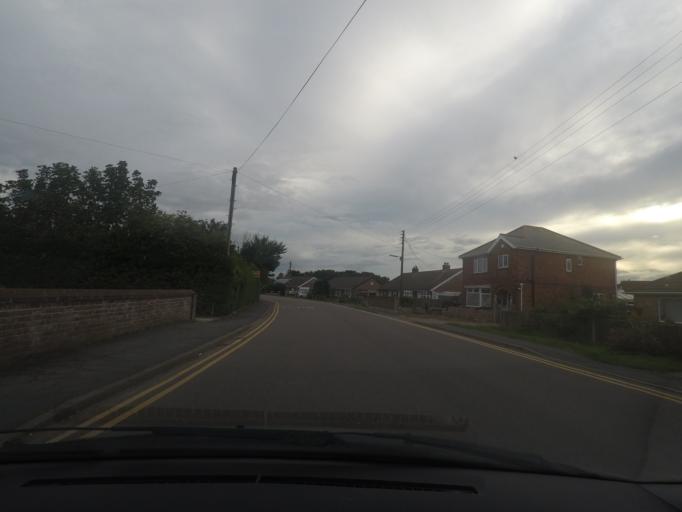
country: GB
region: England
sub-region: Lincolnshire
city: Chapel Saint Leonards
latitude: 53.2225
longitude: 0.3358
